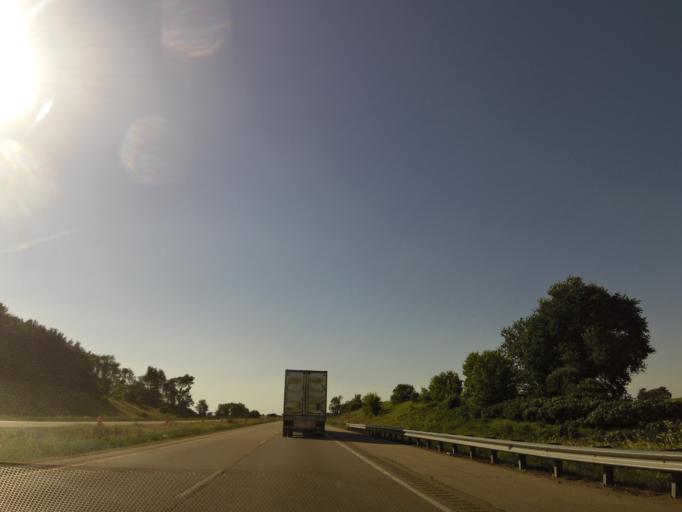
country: US
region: Wisconsin
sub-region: Dane County
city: Deerfield
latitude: 42.9679
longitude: -89.1065
